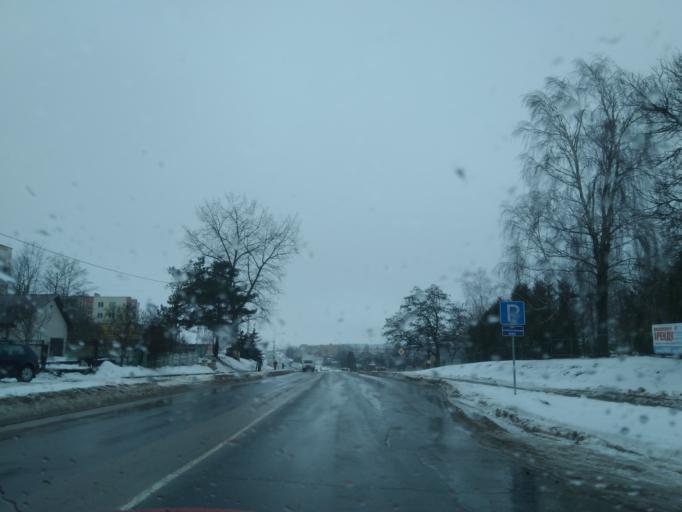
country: BY
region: Minsk
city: Nyasvizh
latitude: 53.2321
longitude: 26.6541
